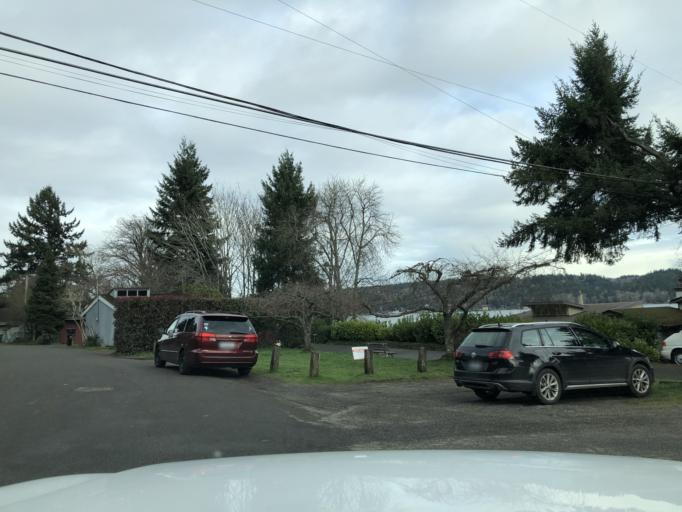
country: US
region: Washington
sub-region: King County
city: Inglewood-Finn Hill
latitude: 47.6993
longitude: -122.2734
